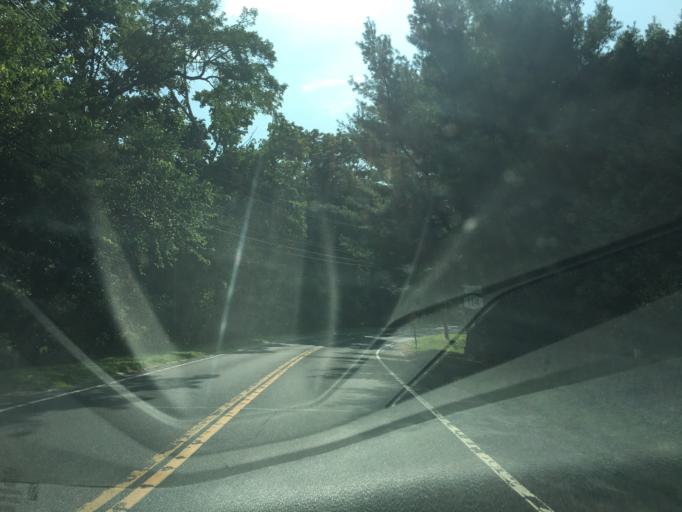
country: US
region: New York
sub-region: Suffolk County
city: Shelter Island
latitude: 41.0761
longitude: -72.3466
